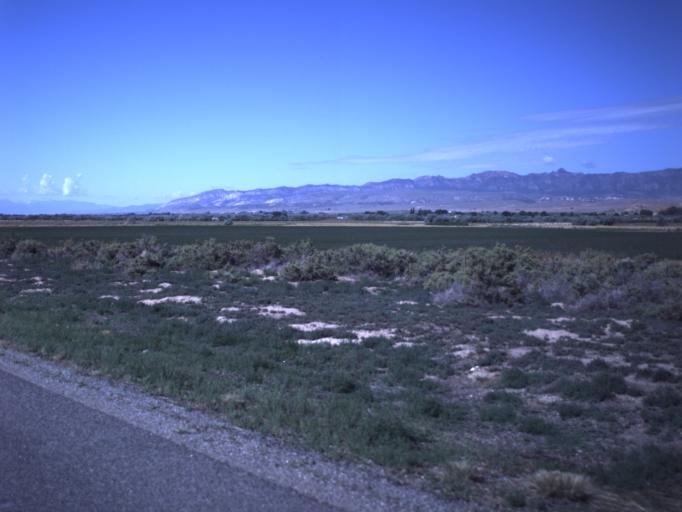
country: US
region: Utah
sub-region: Sevier County
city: Salina
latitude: 39.0067
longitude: -111.8381
